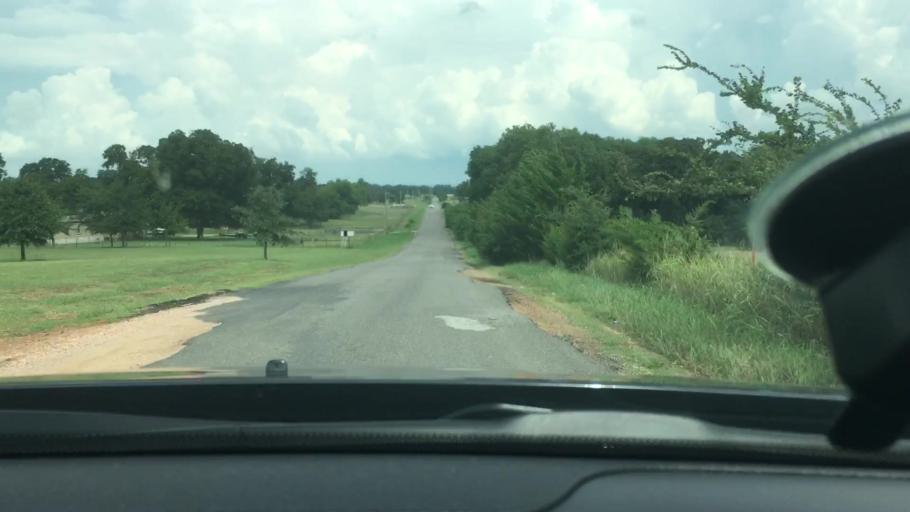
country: US
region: Oklahoma
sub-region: Carter County
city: Dickson
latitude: 34.1898
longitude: -96.8982
